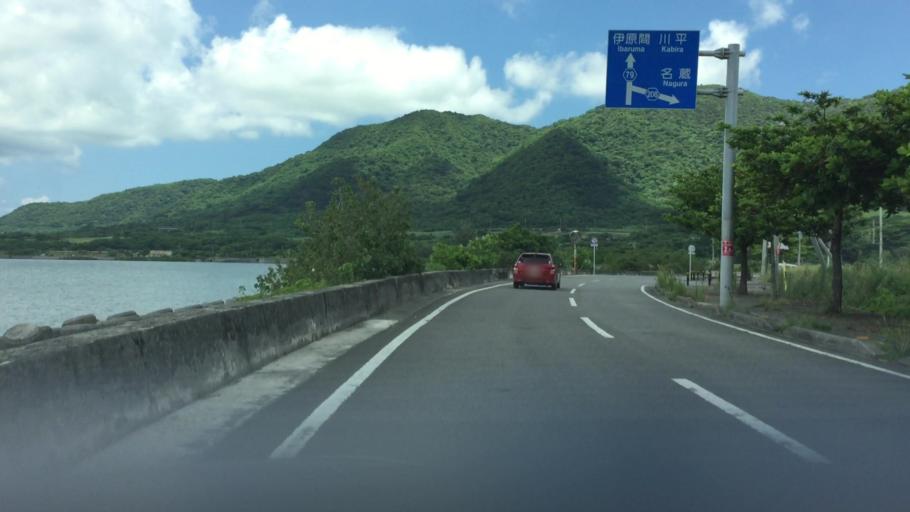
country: JP
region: Okinawa
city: Ishigaki
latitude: 24.4090
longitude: 124.1441
